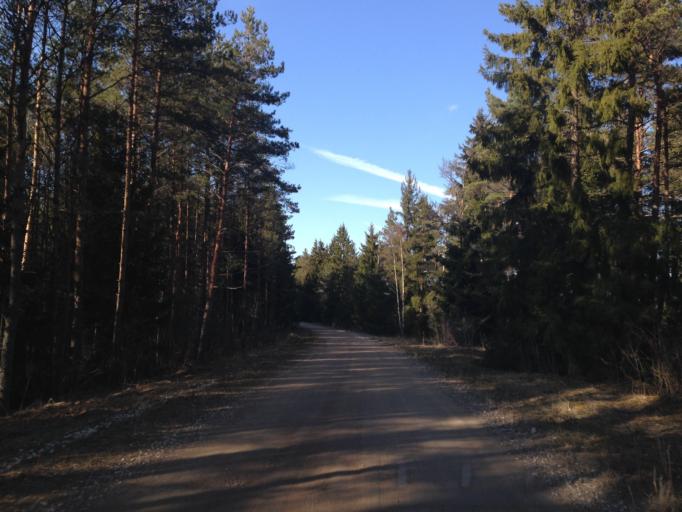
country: EE
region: Harju
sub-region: Nissi vald
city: Turba
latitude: 59.1069
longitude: 24.1571
